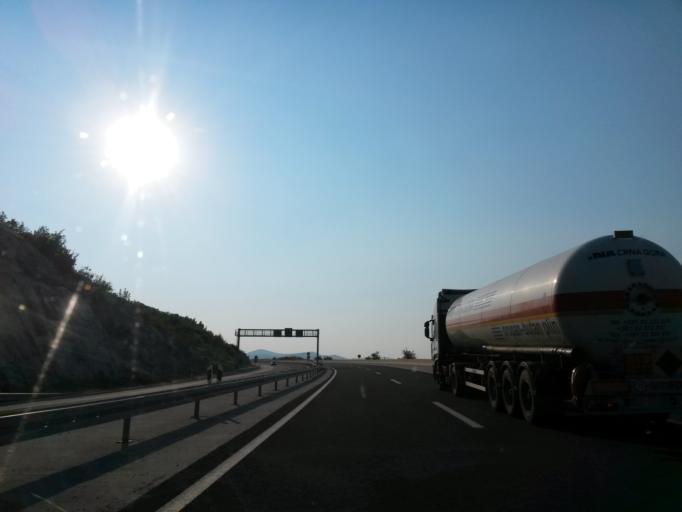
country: HR
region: Splitsko-Dalmatinska
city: Greda
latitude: 43.5810
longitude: 16.6618
